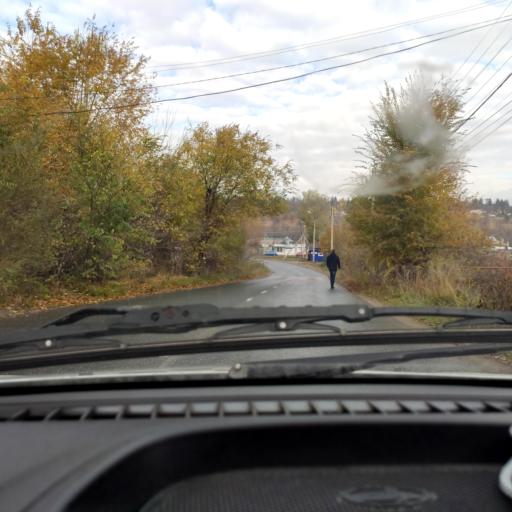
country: RU
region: Samara
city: Zhigulevsk
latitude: 53.4651
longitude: 49.6207
